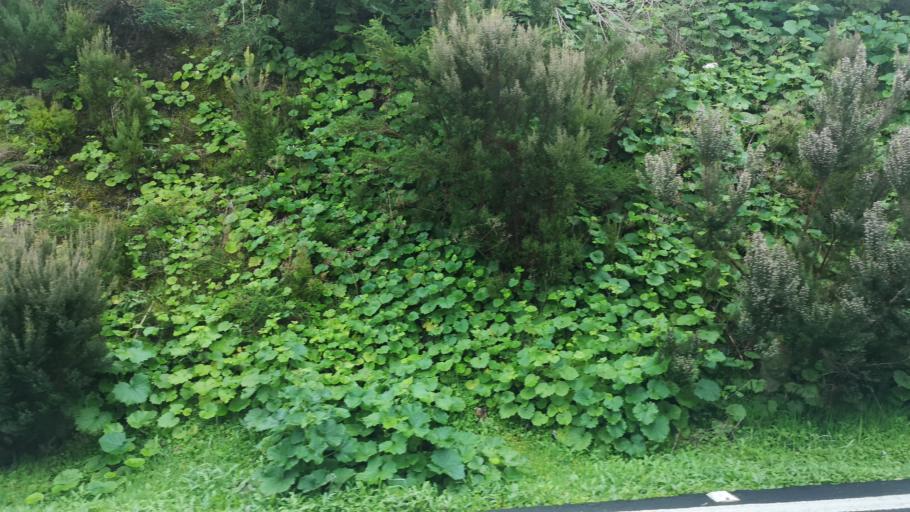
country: ES
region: Canary Islands
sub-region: Provincia de Santa Cruz de Tenerife
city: Alajero
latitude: 28.1078
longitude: -17.2395
